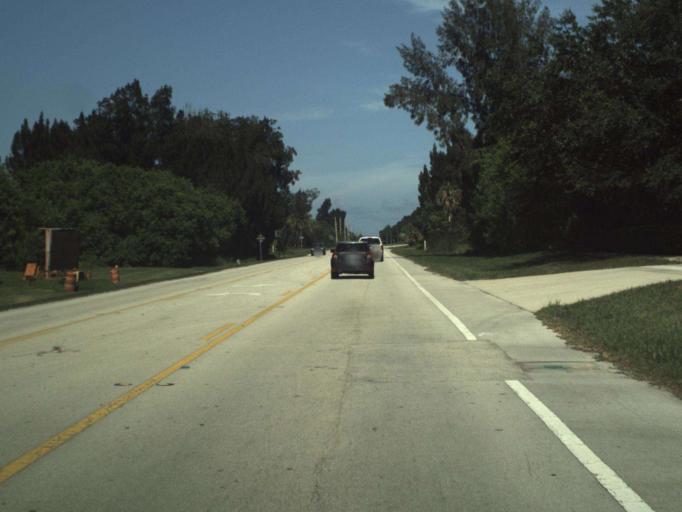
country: US
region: Florida
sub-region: Indian River County
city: Wabasso Beach
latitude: 27.7633
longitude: -80.4082
